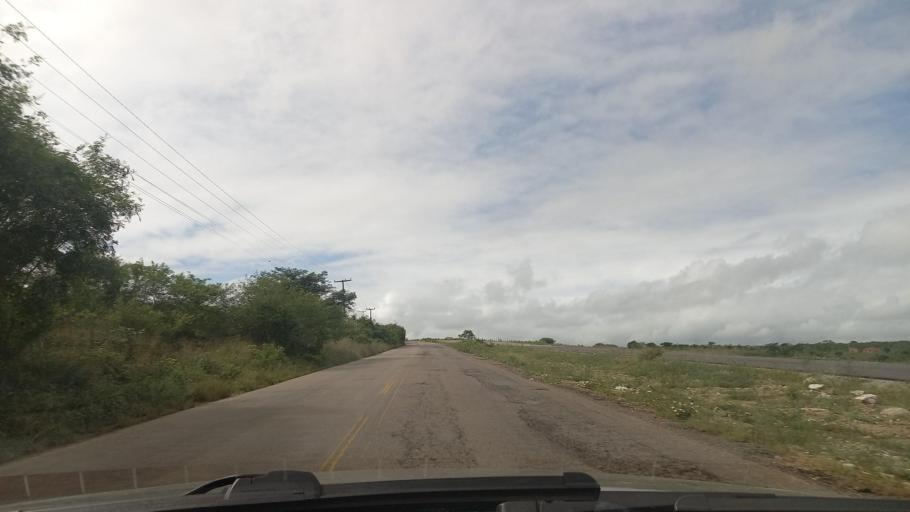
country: BR
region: Alagoas
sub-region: Batalha
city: Batalha
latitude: -9.6619
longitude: -37.1706
